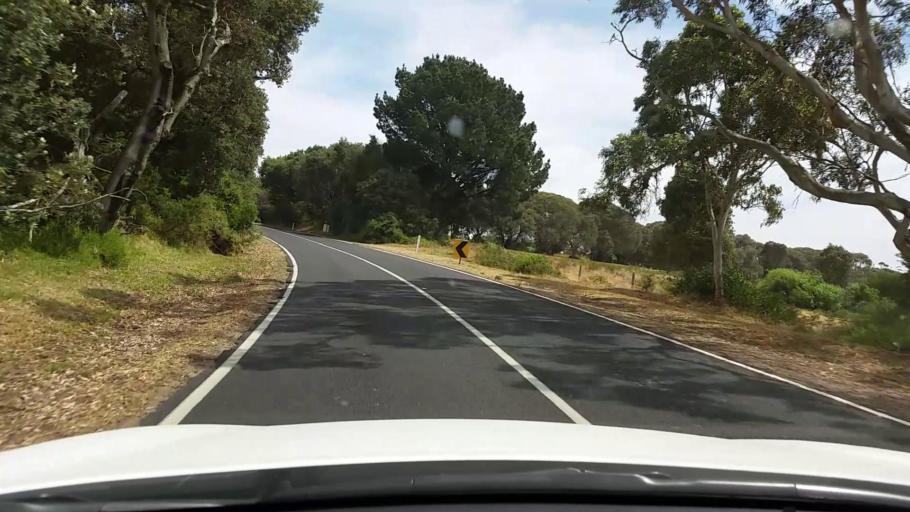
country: AU
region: Victoria
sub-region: Mornington Peninsula
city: Saint Andrews Beach
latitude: -38.4701
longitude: 144.9235
